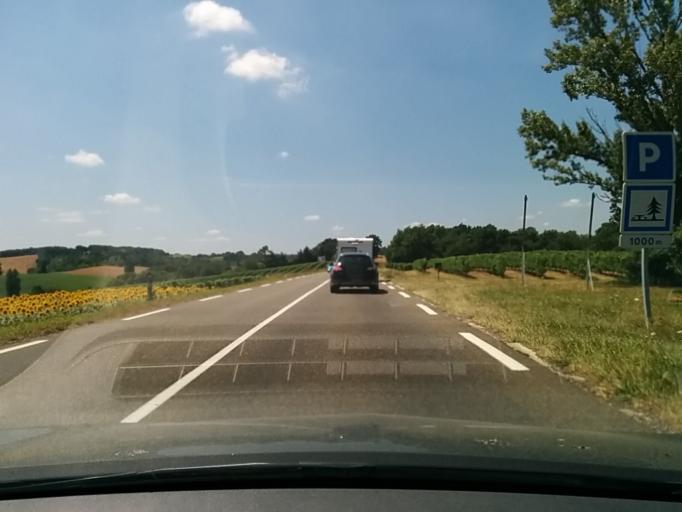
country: FR
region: Midi-Pyrenees
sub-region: Departement du Gers
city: Vic-Fezensac
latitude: 43.7582
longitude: 0.2176
